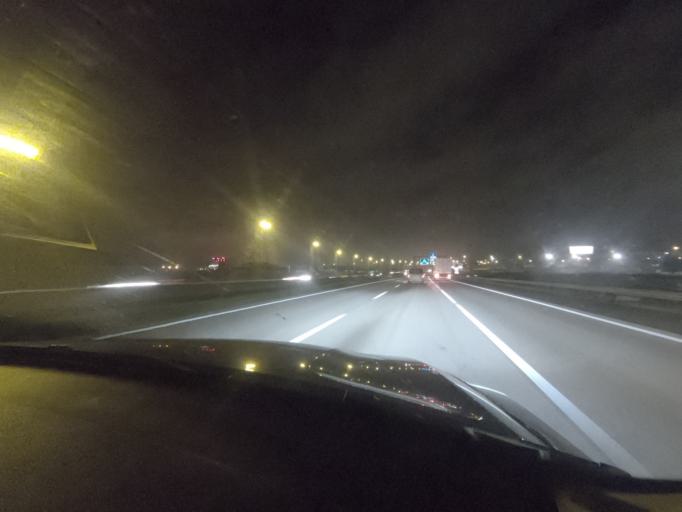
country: PT
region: Lisbon
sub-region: Alenquer
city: Carregado
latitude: 39.0292
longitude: -8.9615
